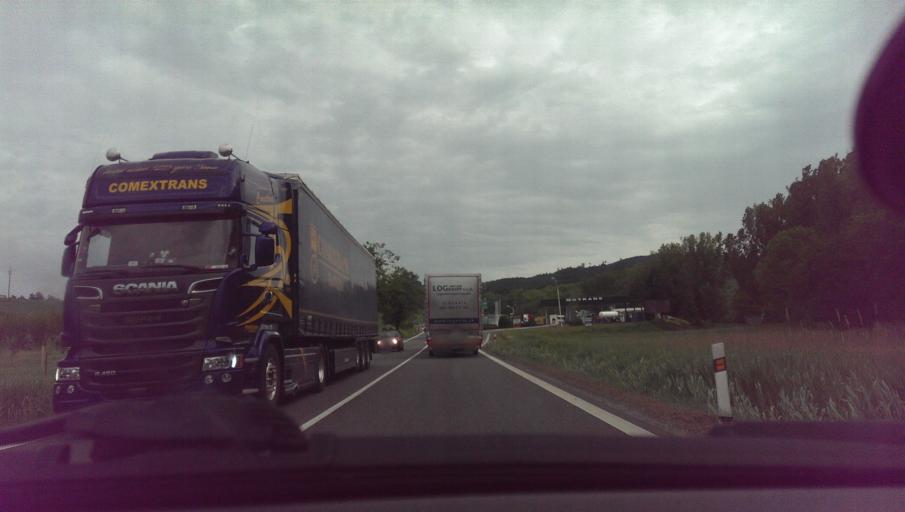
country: CZ
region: Zlin
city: Korycany
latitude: 49.1522
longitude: 17.2189
